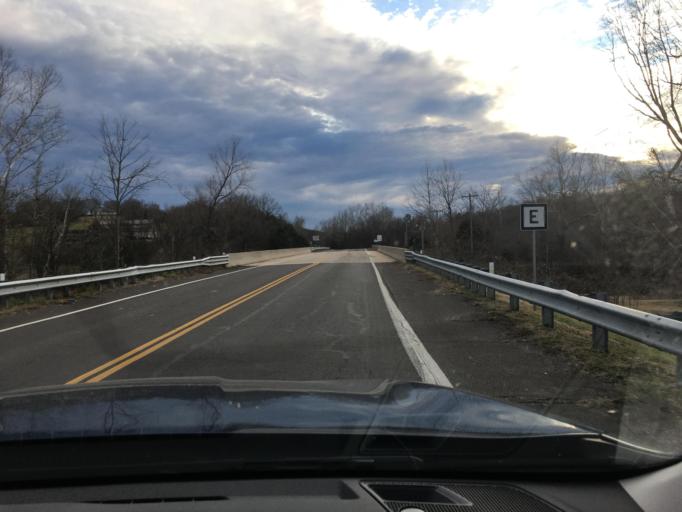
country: US
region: Missouri
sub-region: Jefferson County
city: De Soto
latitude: 38.1153
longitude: -90.5595
